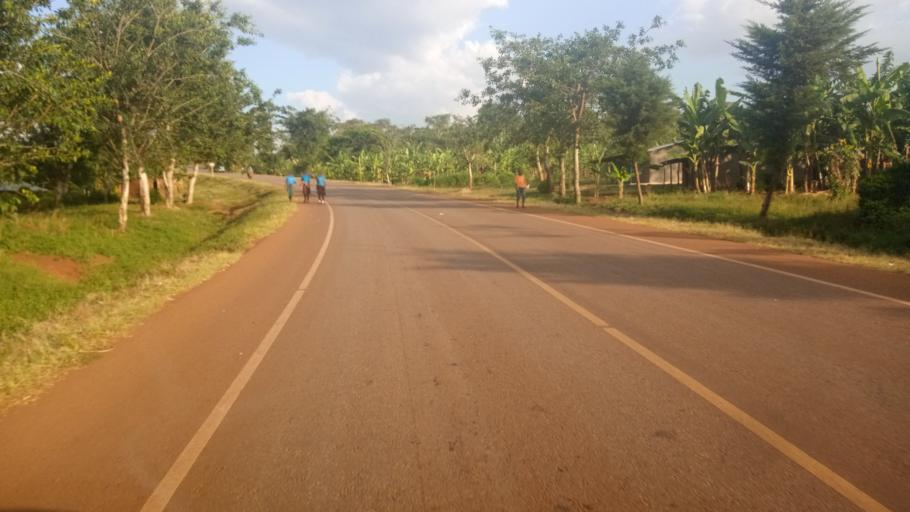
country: UG
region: Eastern Region
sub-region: Sironko District
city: Sironko
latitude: 1.3284
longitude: 34.3266
